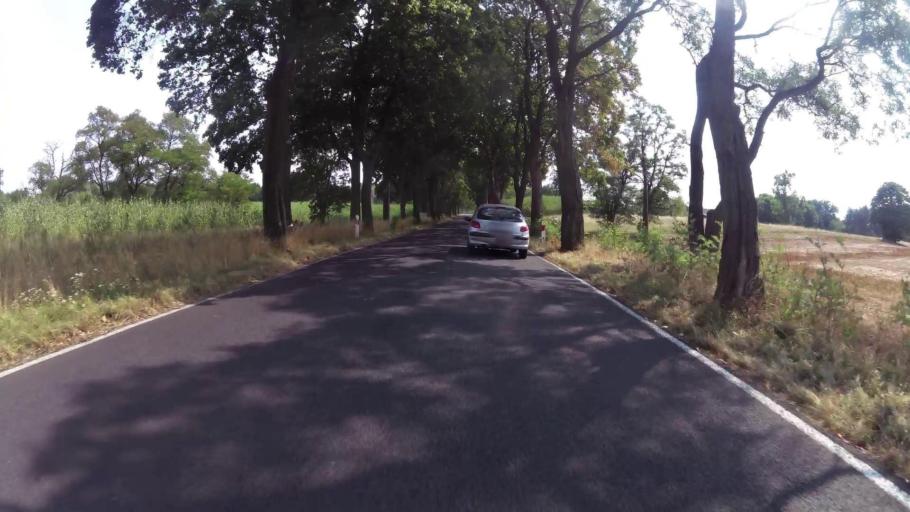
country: PL
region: West Pomeranian Voivodeship
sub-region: Powiat gryfinski
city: Moryn
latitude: 52.8245
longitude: 14.4274
